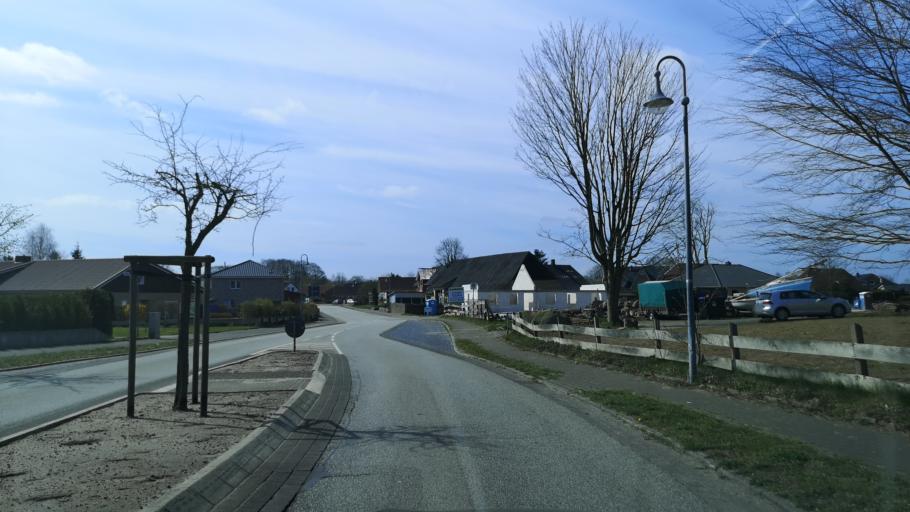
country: DE
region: Schleswig-Holstein
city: Hamdorf
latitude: 54.2317
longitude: 9.5191
